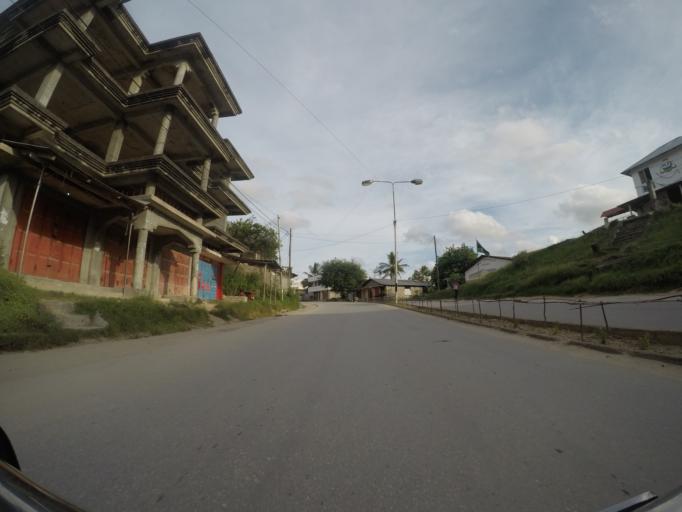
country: TZ
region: Pemba South
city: Chake Chake
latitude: -5.2481
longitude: 39.7706
